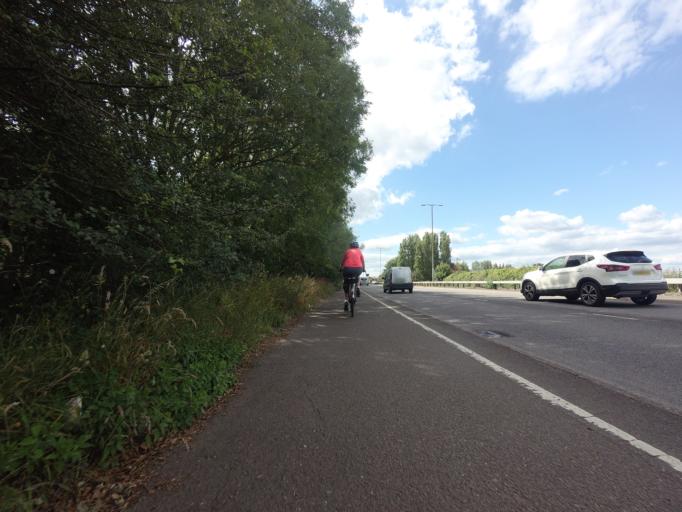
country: GB
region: England
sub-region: East Sussex
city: Eastbourne
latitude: 50.7929
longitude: 0.2912
